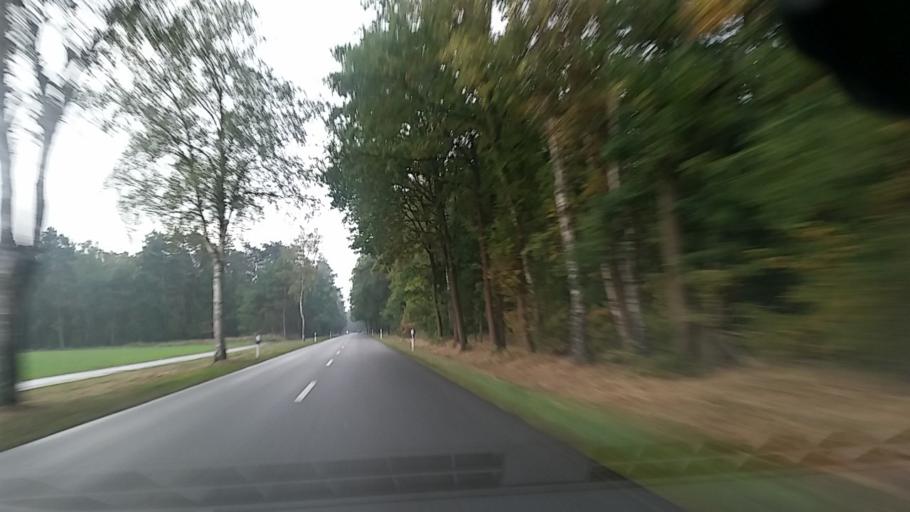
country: DE
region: Lower Saxony
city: Bokensdorf
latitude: 52.5348
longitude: 10.7172
